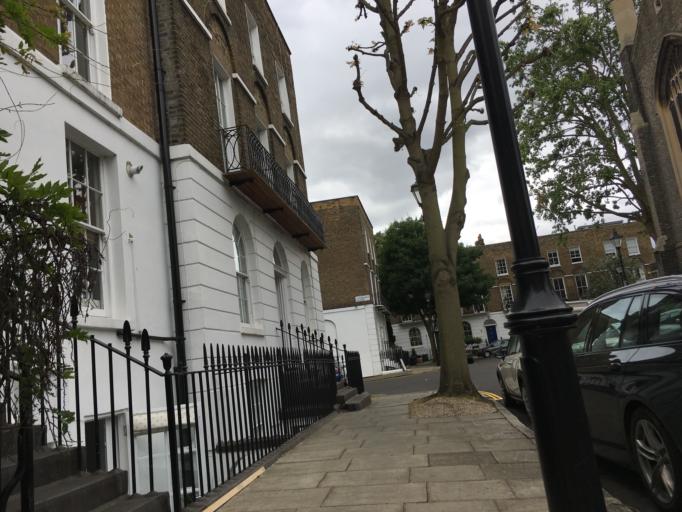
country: GB
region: England
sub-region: Greater London
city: Islington
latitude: 51.5376
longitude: -0.1078
